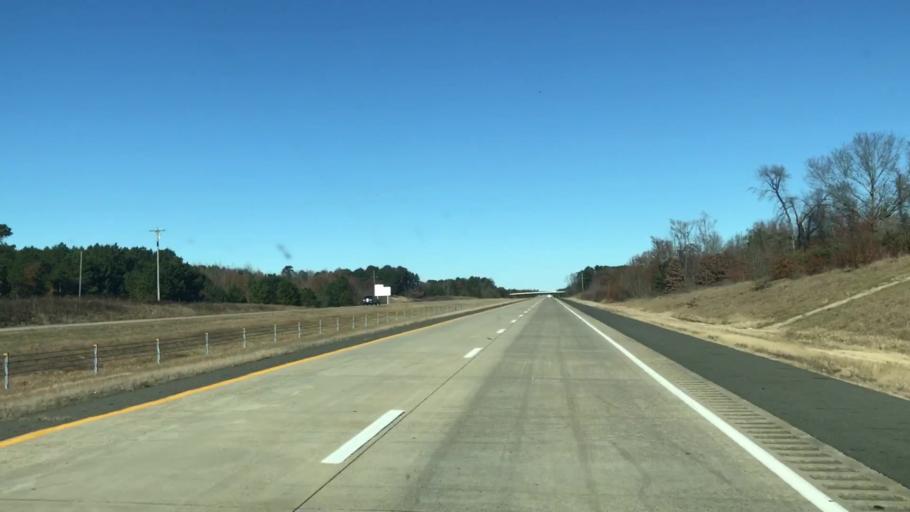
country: US
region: Texas
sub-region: Bowie County
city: Texarkana
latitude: 33.2833
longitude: -93.9115
